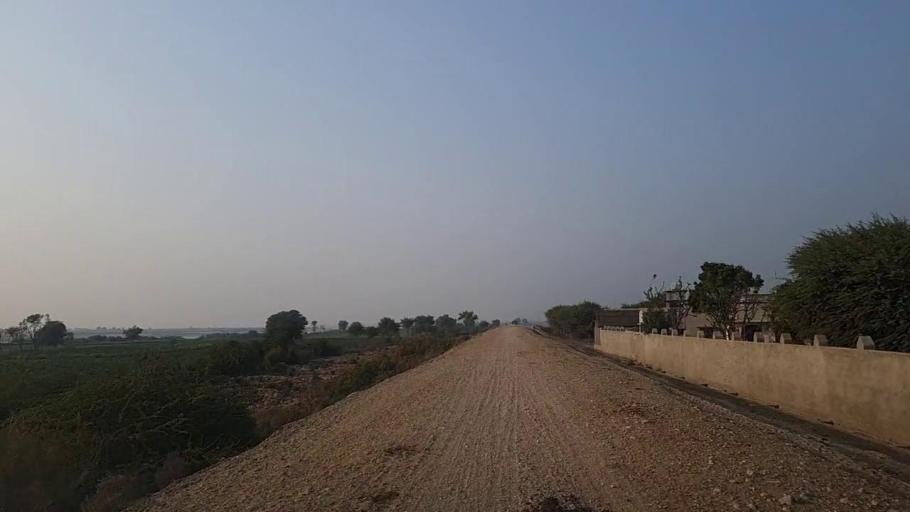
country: PK
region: Sindh
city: Sann
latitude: 26.1241
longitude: 68.1428
